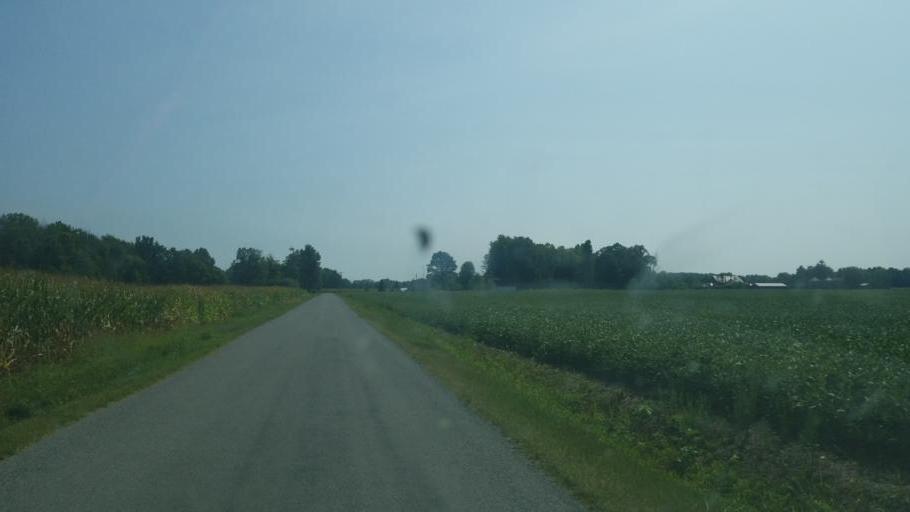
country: US
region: Ohio
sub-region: Crawford County
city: Crestline
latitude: 40.8260
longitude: -82.7446
